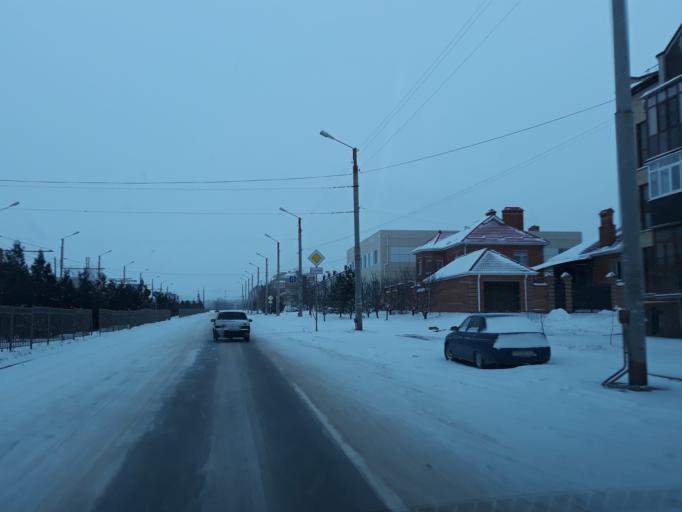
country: RU
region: Rostov
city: Taganrog
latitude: 47.2739
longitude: 38.9182
